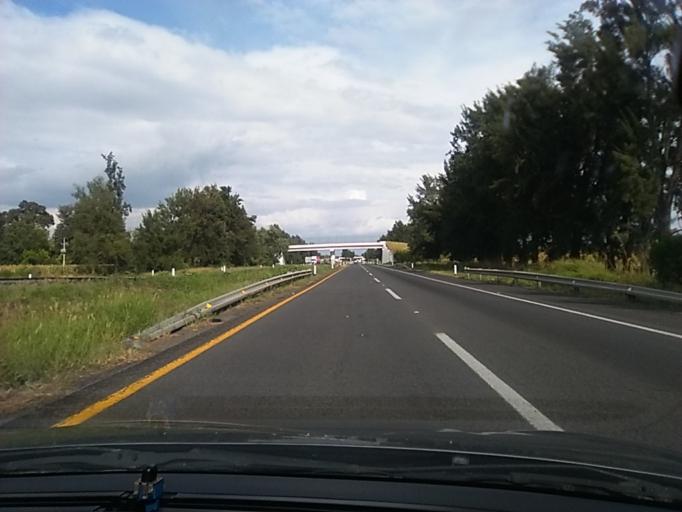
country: MX
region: Jalisco
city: La Barca
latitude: 20.3219
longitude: -102.5182
